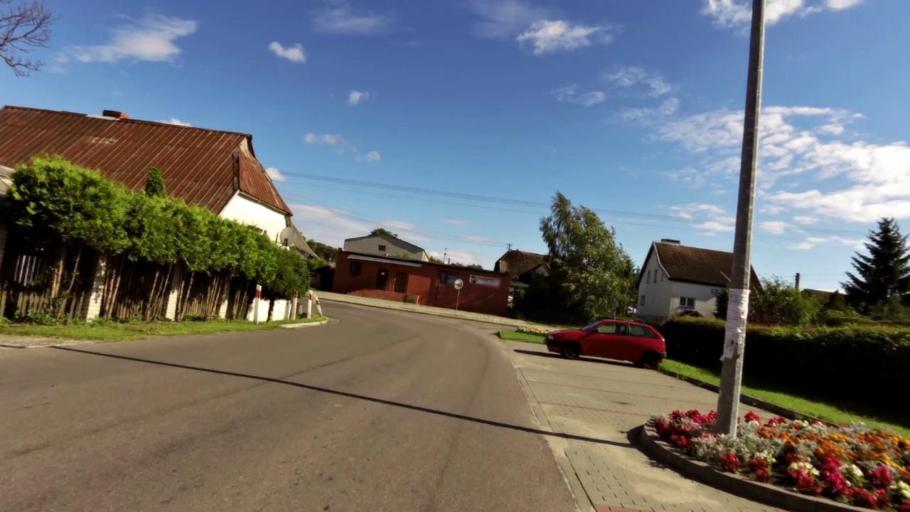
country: PL
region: West Pomeranian Voivodeship
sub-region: Powiat slawienski
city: Slawno
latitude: 54.4347
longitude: 16.7334
